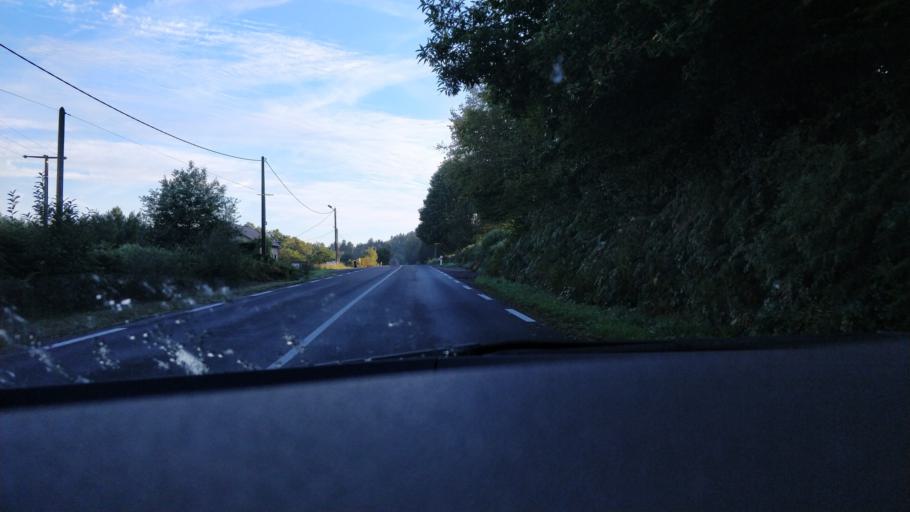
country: FR
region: Limousin
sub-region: Departement de la Haute-Vienne
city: Sauviat-sur-Vige
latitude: 45.8913
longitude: 1.5749
